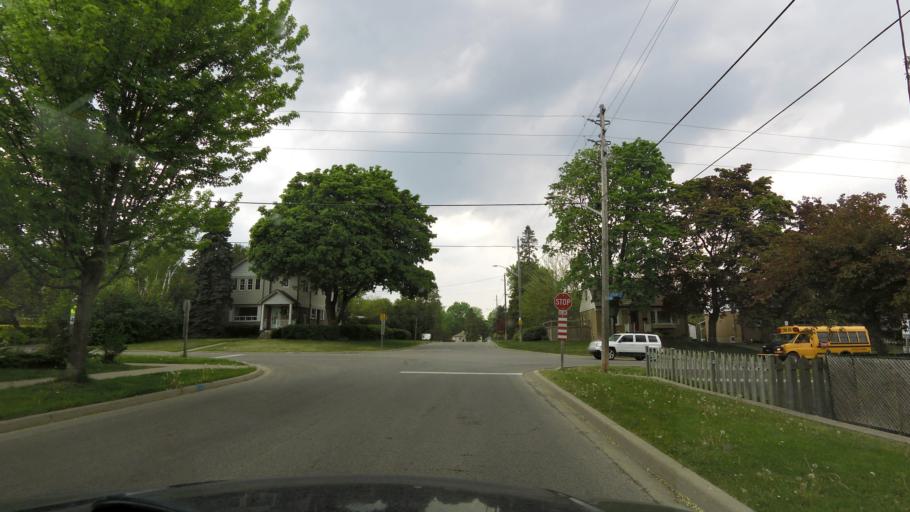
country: CA
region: Ontario
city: Mississauga
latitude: 43.5746
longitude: -79.5797
